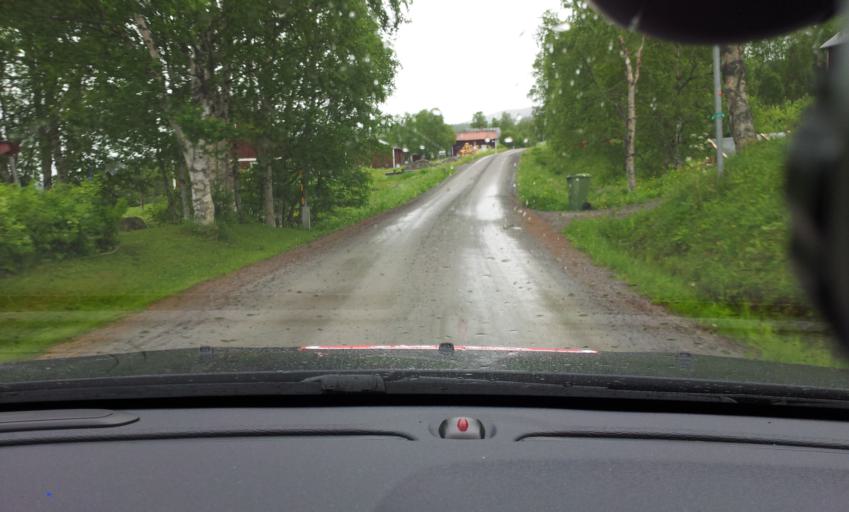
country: SE
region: Jaemtland
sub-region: Are Kommun
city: Are
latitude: 63.4691
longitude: 12.8099
